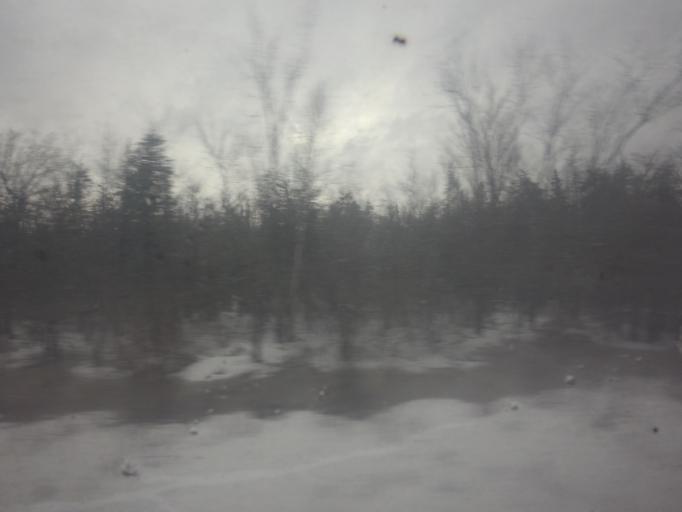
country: CA
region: Ontario
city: Bells Corners
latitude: 45.1275
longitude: -75.8632
